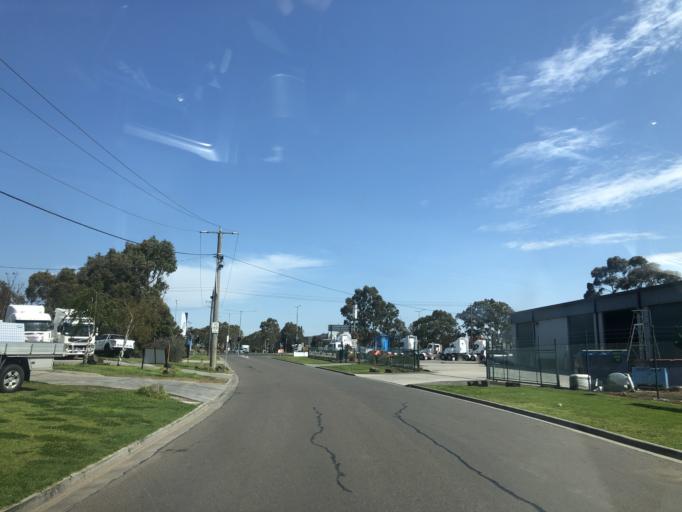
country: AU
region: Victoria
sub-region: Casey
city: Hampton Park
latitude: -38.0200
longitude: 145.2403
